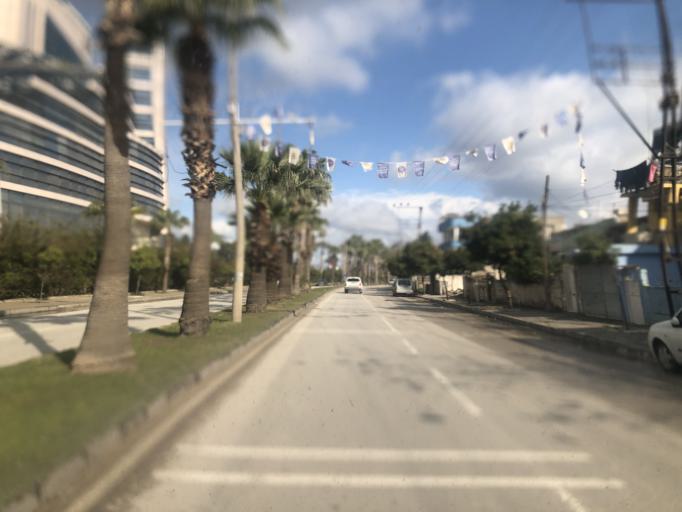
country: TR
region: Adana
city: Adana
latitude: 36.9936
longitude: 35.3400
